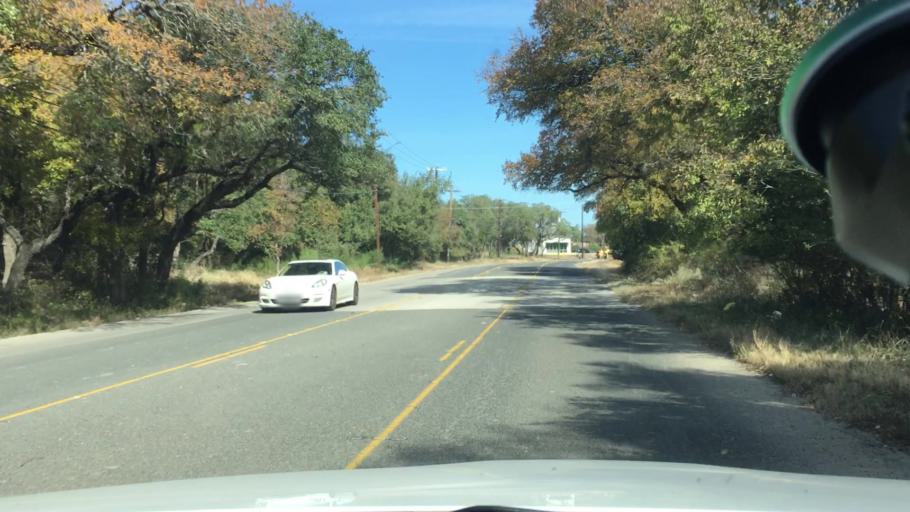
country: US
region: Texas
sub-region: Bexar County
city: Hollywood Park
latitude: 29.5963
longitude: -98.4232
